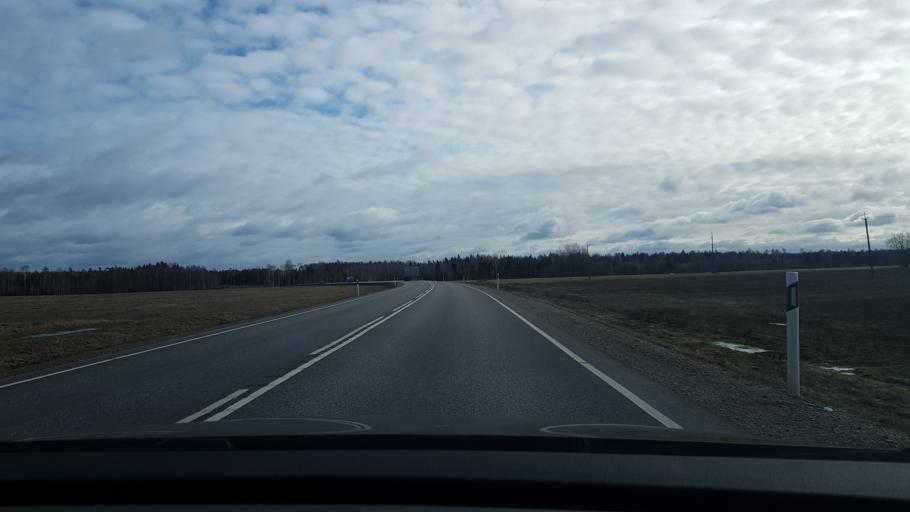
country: EE
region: Viljandimaa
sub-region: Moisakuela linn
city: Moisakula
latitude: 58.1301
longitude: 25.1219
